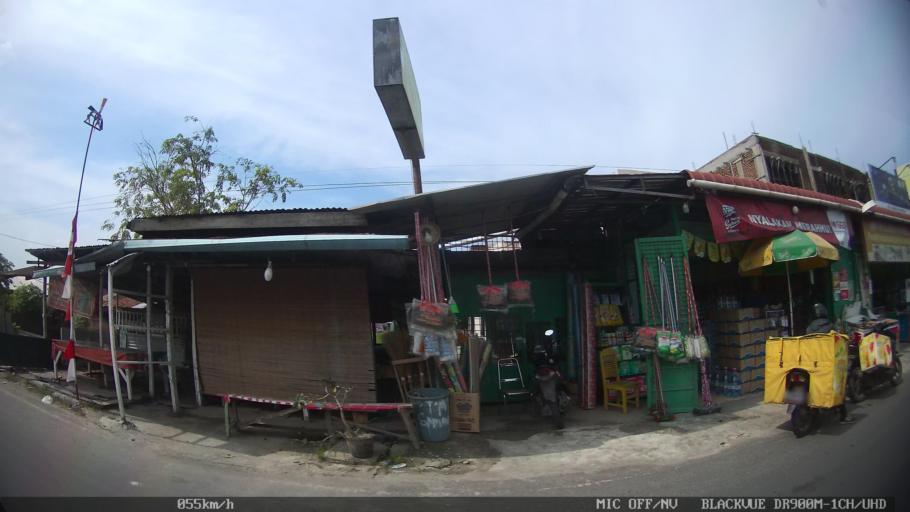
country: ID
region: North Sumatra
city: Percut
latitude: 3.6117
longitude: 98.8177
